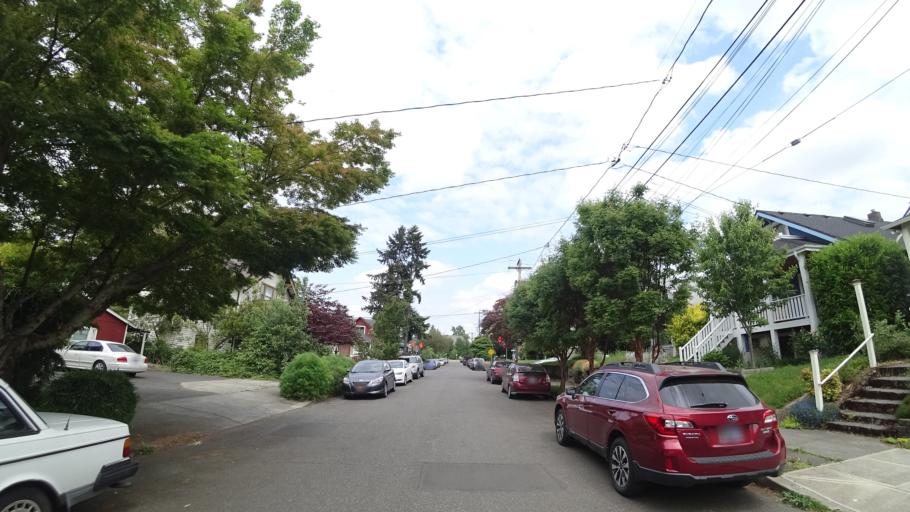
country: US
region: Oregon
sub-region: Multnomah County
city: Portland
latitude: 45.4957
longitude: -122.6386
